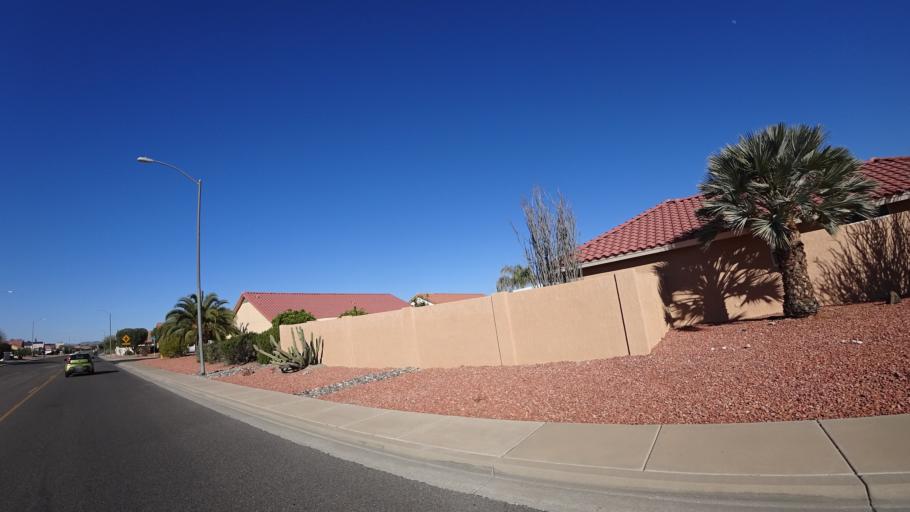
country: US
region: Arizona
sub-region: Maricopa County
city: Sun City West
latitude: 33.6775
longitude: -112.3810
